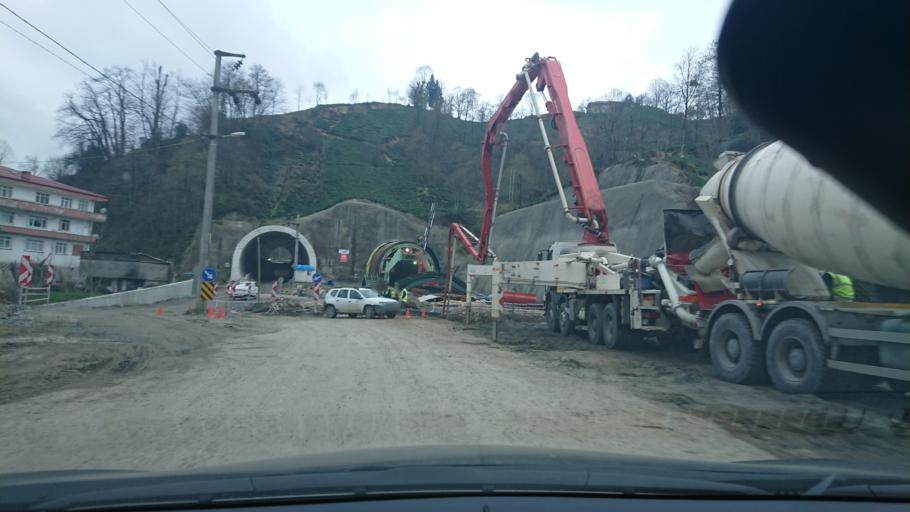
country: TR
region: Rize
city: Rize
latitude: 41.0173
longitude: 40.4964
